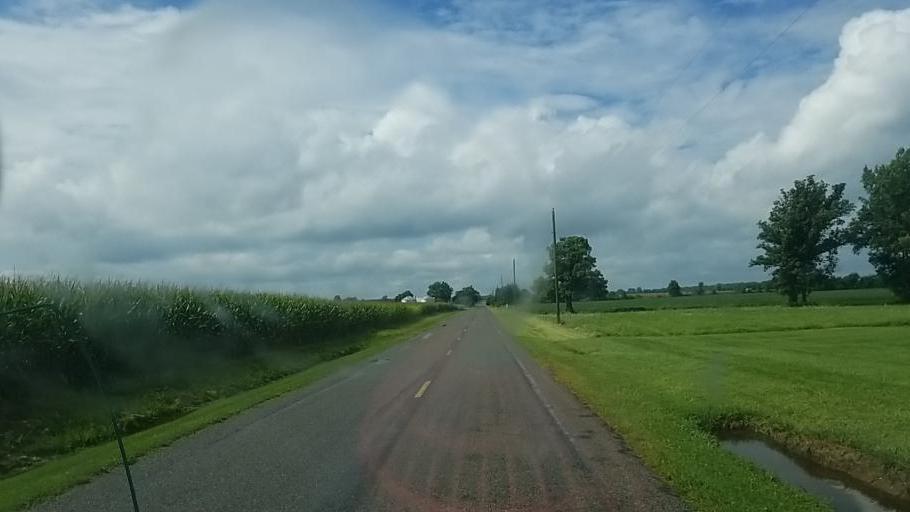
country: US
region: Ohio
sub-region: Hardin County
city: Kenton
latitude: 40.4798
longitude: -83.5115
